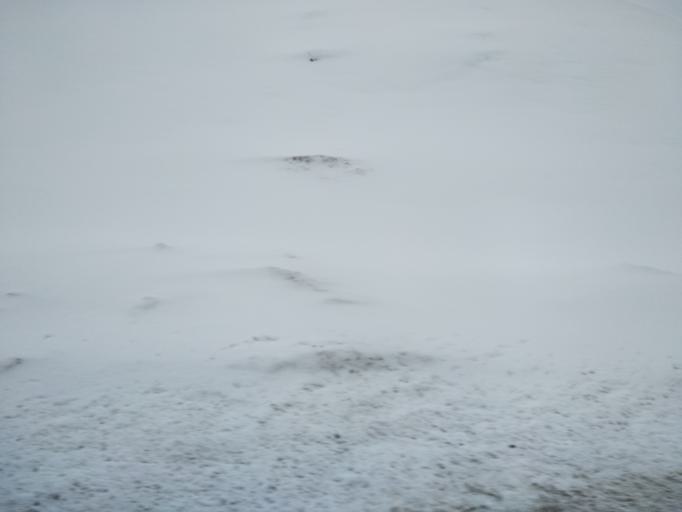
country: TR
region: Erzincan
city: Catalarmut
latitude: 39.8879
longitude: 39.3483
